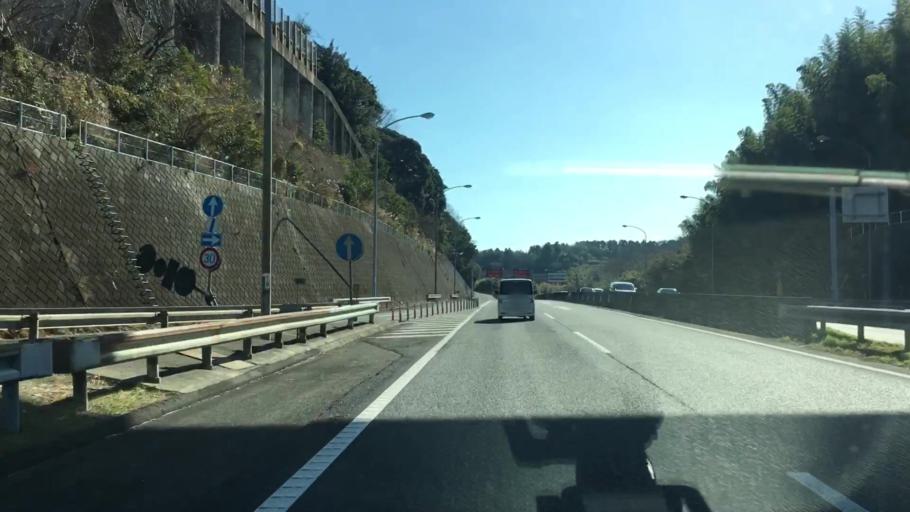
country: JP
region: Kanagawa
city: Kamakura
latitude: 35.3678
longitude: 139.5960
